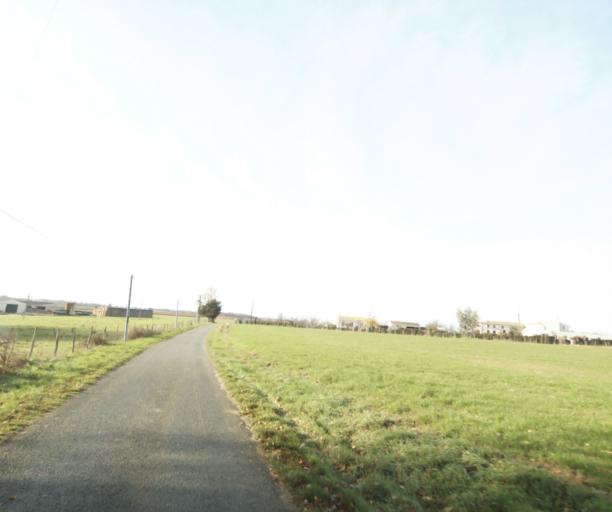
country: FR
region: Poitou-Charentes
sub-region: Departement de la Charente-Maritime
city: Chaniers
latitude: 45.7403
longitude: -0.5166
